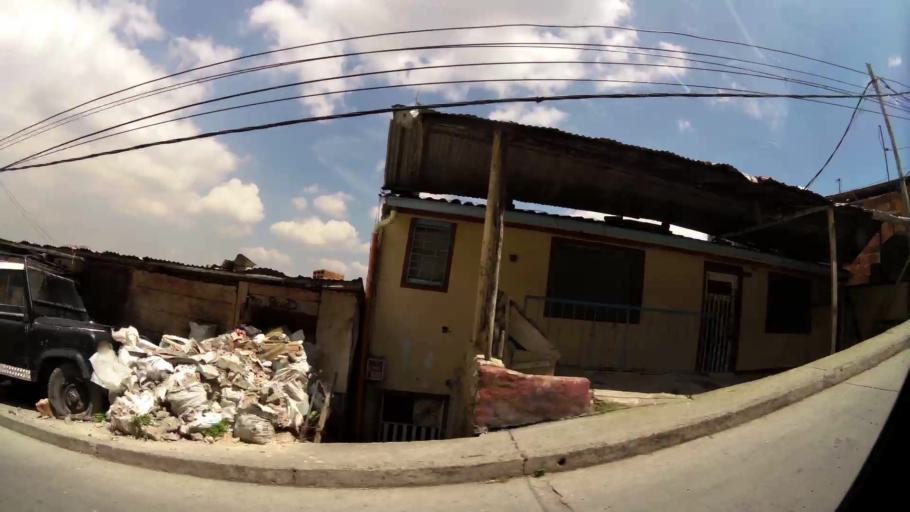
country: CO
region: Cundinamarca
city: La Calera
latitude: 4.7332
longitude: -74.0179
